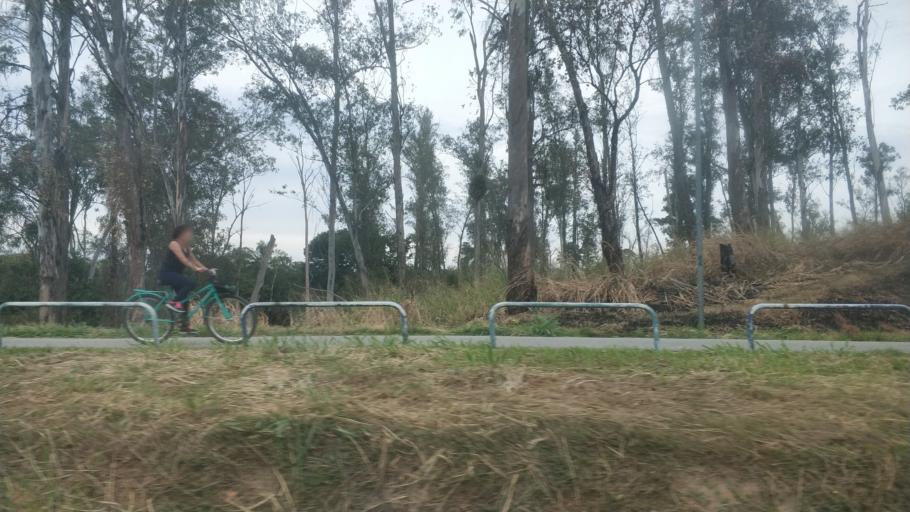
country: BR
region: Rio de Janeiro
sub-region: Seropedica
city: Seropedica
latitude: -22.7529
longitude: -43.6944
